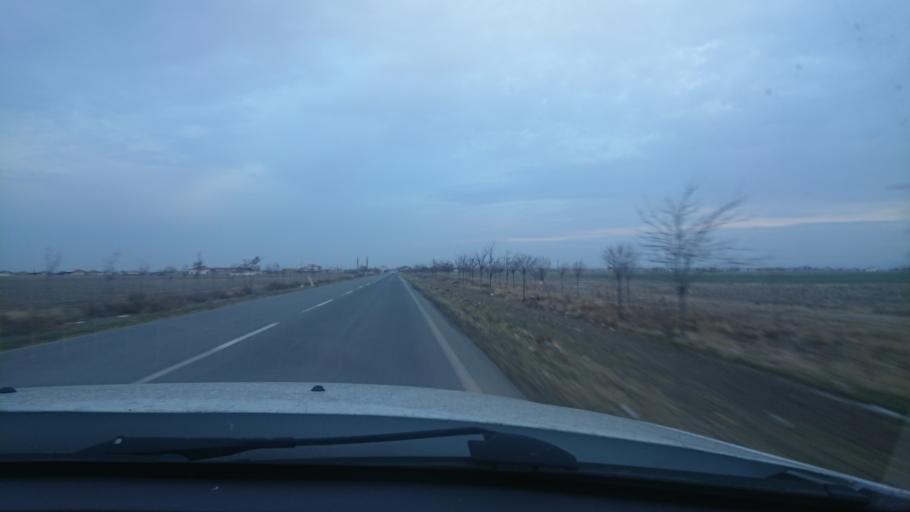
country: TR
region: Aksaray
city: Yesilova
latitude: 38.3259
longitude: 33.7532
